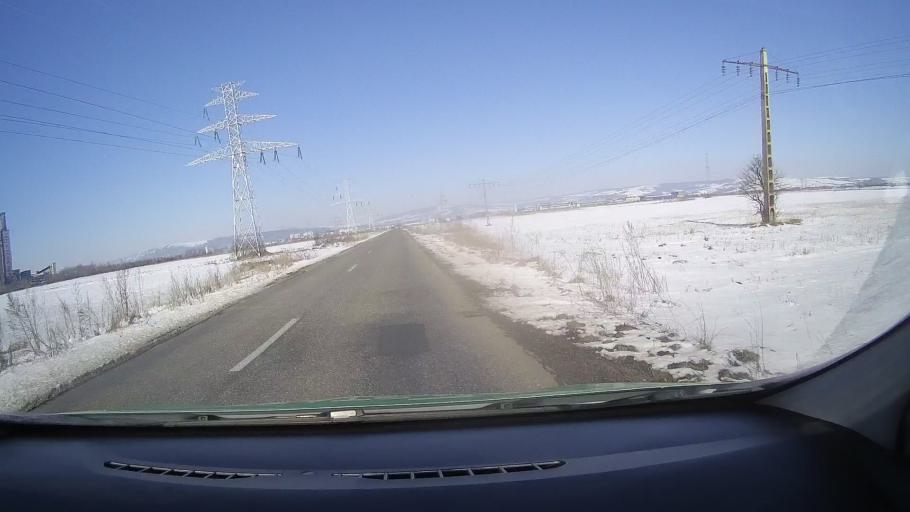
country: RO
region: Brasov
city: Fogarasch
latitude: 45.8120
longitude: 24.9890
